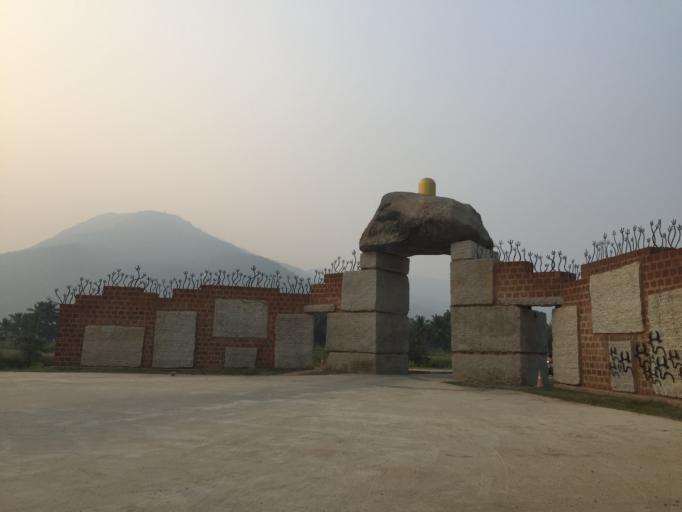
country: IN
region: Tamil Nadu
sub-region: Coimbatore
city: Perur
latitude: 10.9629
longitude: 76.7423
